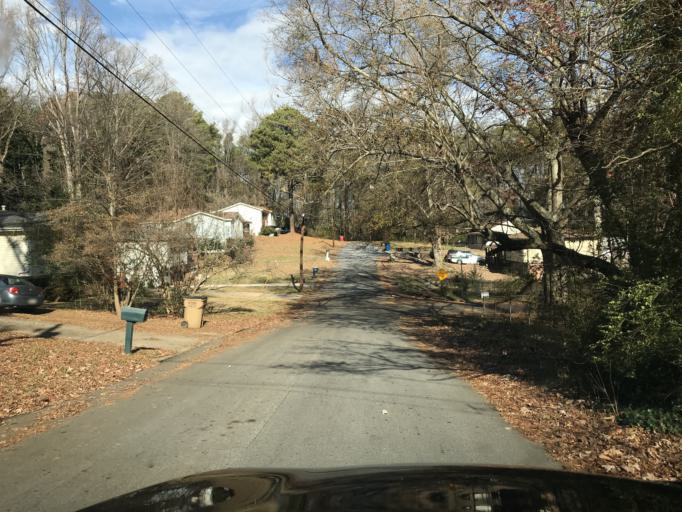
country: US
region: Georgia
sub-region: Clayton County
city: Morrow
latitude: 33.5820
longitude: -84.3738
